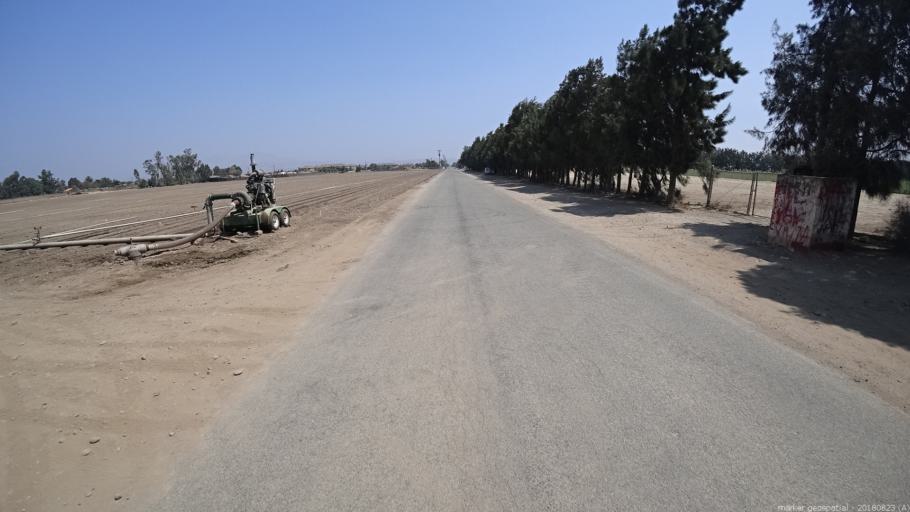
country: US
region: California
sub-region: Monterey County
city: Greenfield
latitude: 36.3106
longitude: -121.2617
